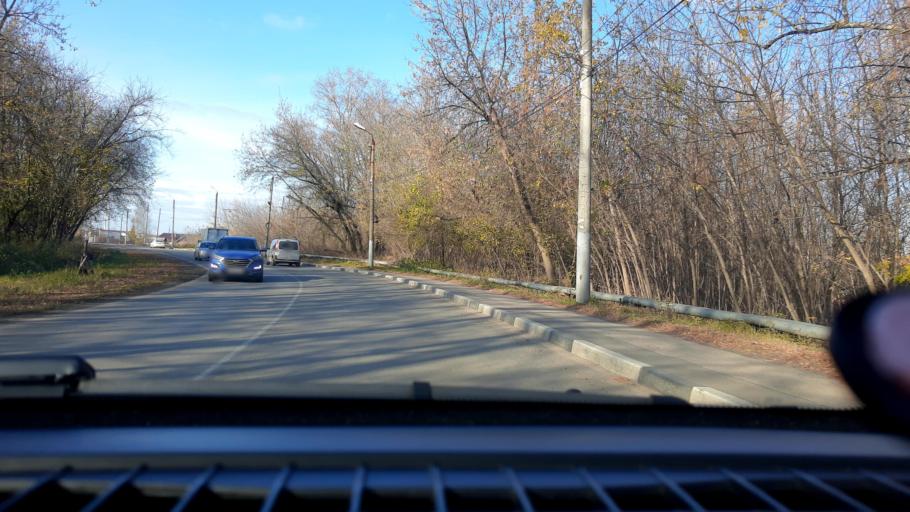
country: RU
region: Nizjnij Novgorod
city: Kstovo
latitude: 56.1611
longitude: 44.2058
